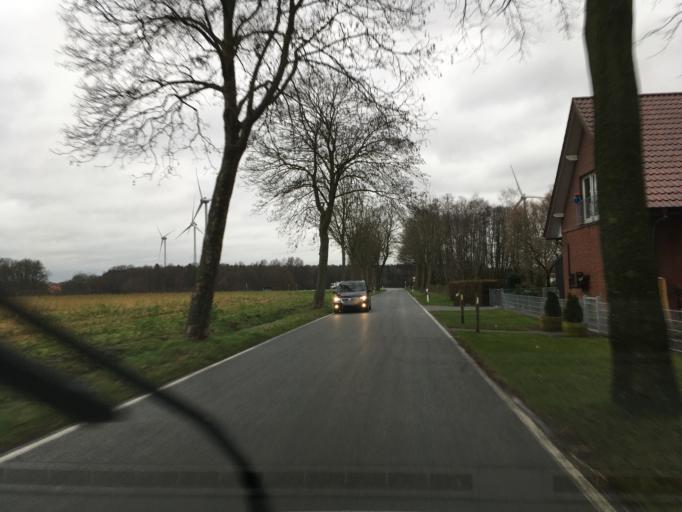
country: DE
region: North Rhine-Westphalia
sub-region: Regierungsbezirk Munster
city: Schoppingen
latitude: 52.0956
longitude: 7.1744
